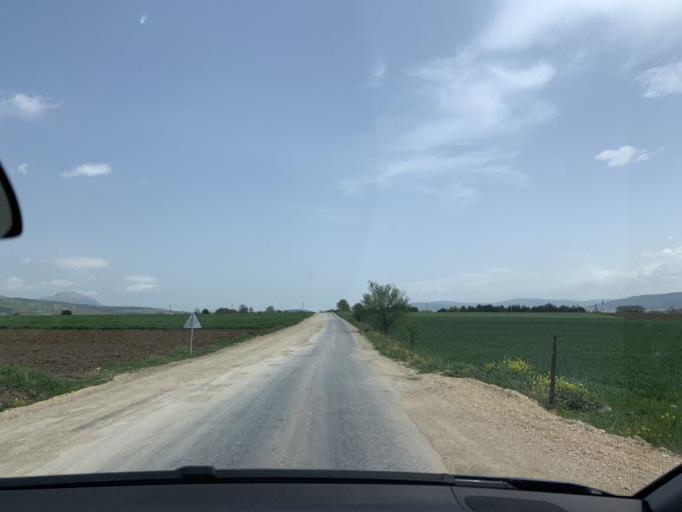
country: TR
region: Bolu
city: Bolu
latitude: 40.7505
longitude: 31.6693
